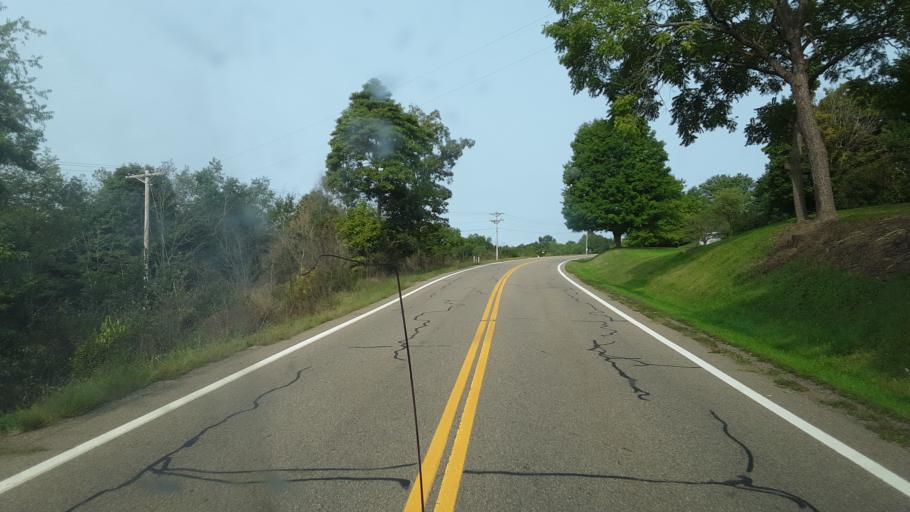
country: US
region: Ohio
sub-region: Coshocton County
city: Coshocton
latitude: 40.4059
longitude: -81.8757
